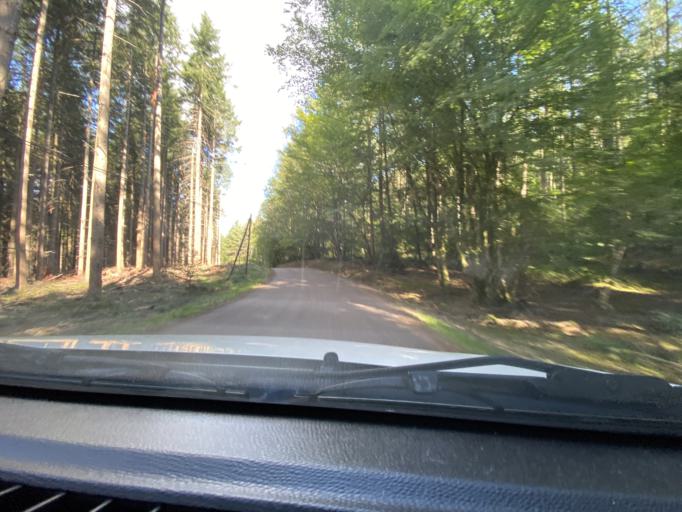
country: FR
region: Bourgogne
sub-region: Departement de la Cote-d'Or
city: Saulieu
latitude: 47.3080
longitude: 4.1863
